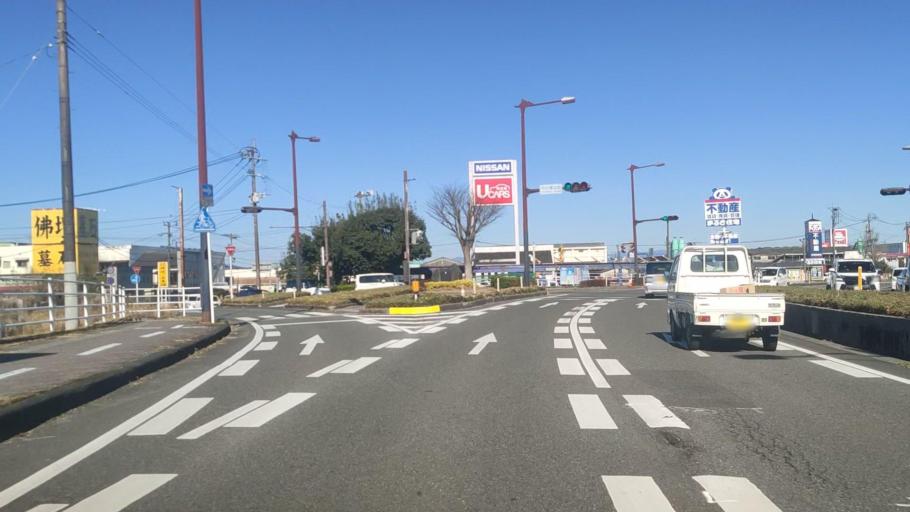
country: JP
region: Miyazaki
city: Miyakonojo
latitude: 31.7511
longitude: 131.0780
